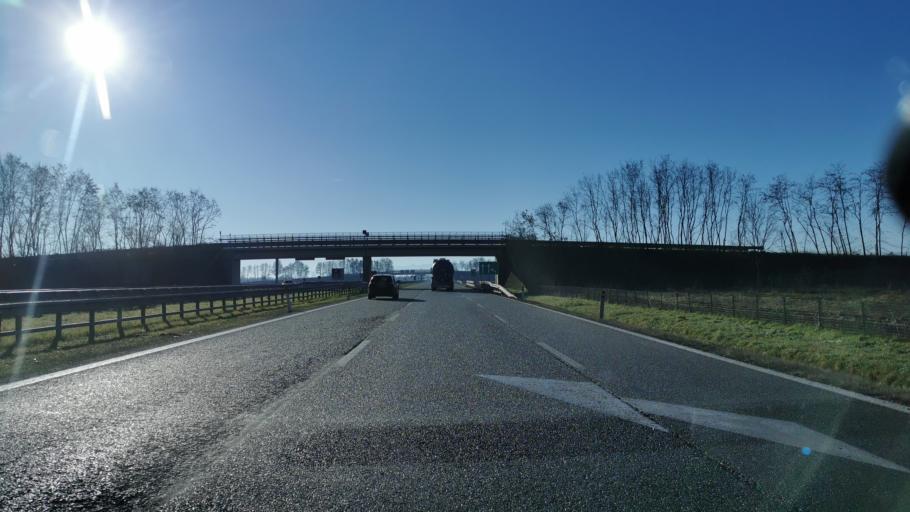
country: IT
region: Piedmont
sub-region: Provincia di Torino
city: Carmagnola
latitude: 44.8488
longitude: 7.7488
